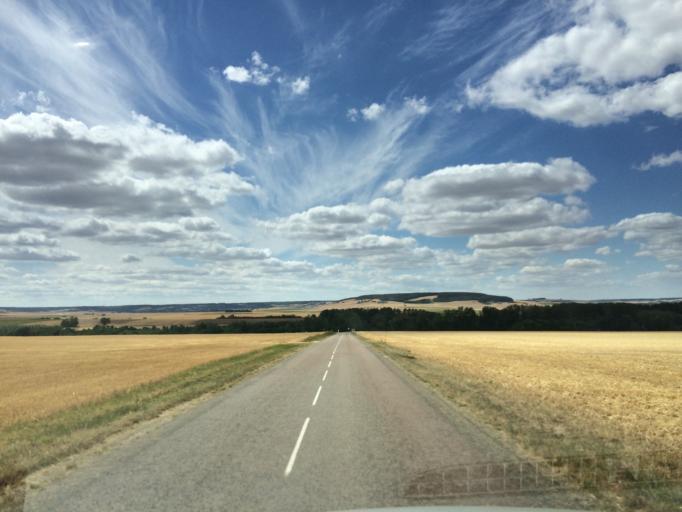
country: FR
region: Bourgogne
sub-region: Departement de l'Yonne
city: Laroche-Saint-Cydroine
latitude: 47.9305
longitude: 3.4505
